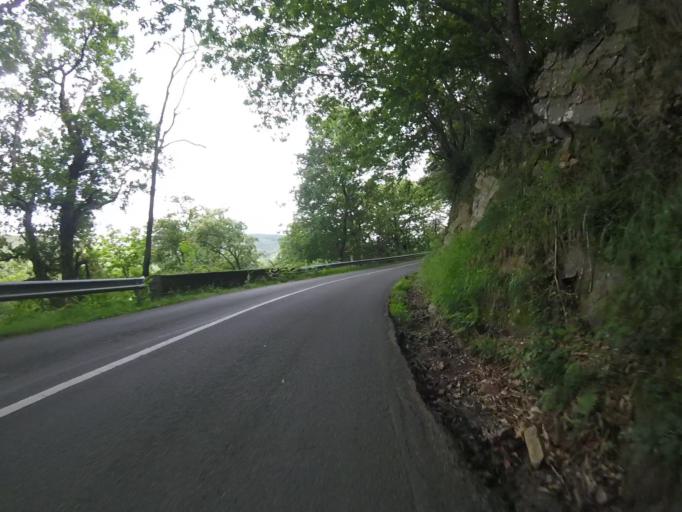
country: ES
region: Basque Country
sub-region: Provincia de Guipuzcoa
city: Errenteria
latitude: 43.2696
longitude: -1.8446
